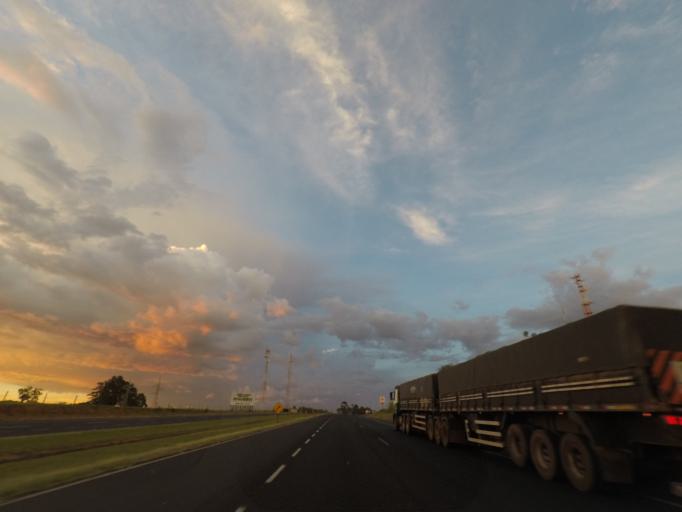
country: BR
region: Minas Gerais
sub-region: Uberaba
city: Uberaba
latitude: -19.5867
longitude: -48.0303
